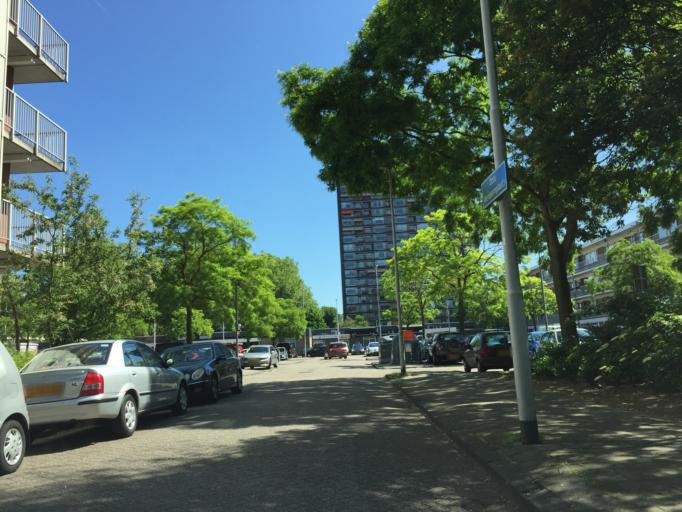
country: NL
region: South Holland
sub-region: Gemeente Rotterdam
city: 's-Gravenland
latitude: 51.9400
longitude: 4.5470
